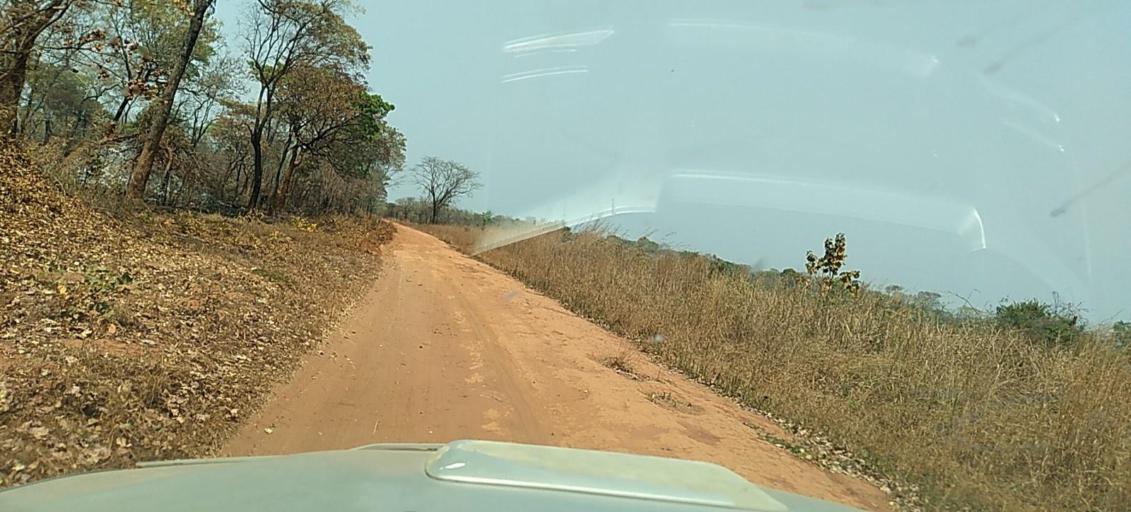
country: ZM
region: North-Western
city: Kasempa
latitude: -13.6225
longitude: 26.2065
